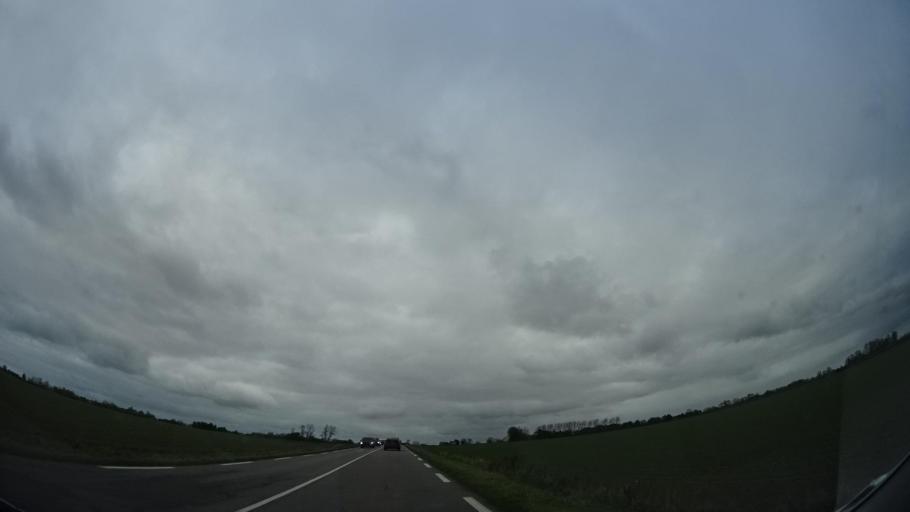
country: FR
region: Haute-Normandie
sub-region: Departement de la Seine-Maritime
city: Saint-Jouin-Bruneval
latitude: 49.6242
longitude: 0.1686
